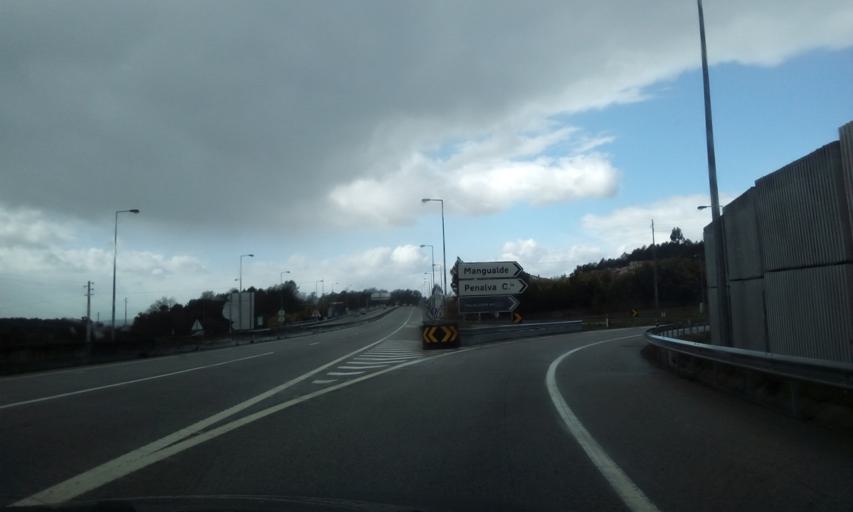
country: PT
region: Viseu
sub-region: Mangualde
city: Mangualde
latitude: 40.6180
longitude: -7.7594
